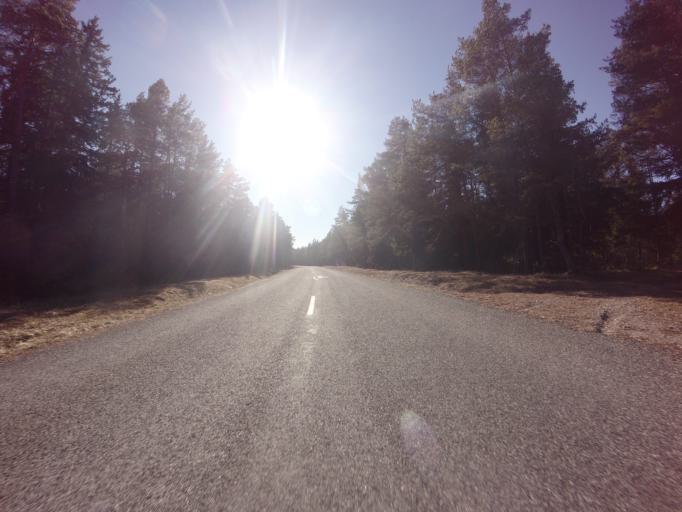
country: EE
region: Saare
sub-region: Kuressaare linn
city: Kuressaare
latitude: 58.5161
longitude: 22.3233
